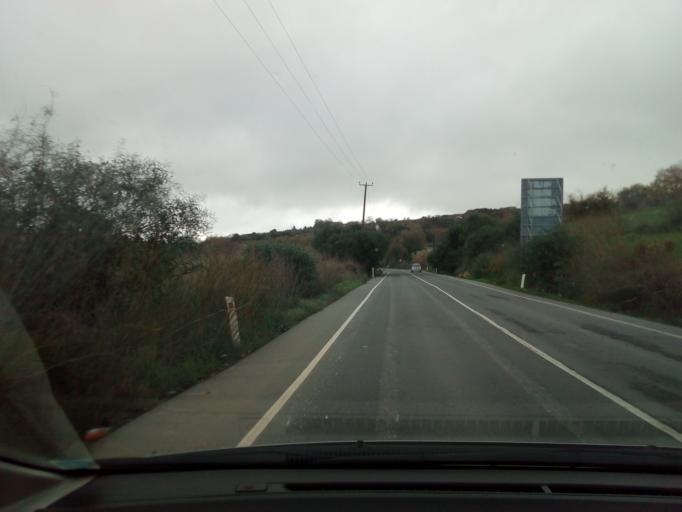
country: CY
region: Pafos
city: Tala
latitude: 34.8955
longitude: 32.4701
